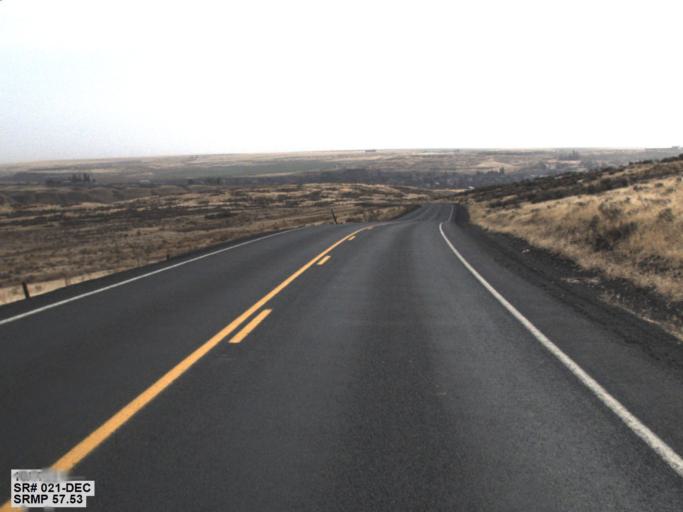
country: US
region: Washington
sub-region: Adams County
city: Ritzville
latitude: 47.3540
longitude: -118.6980
